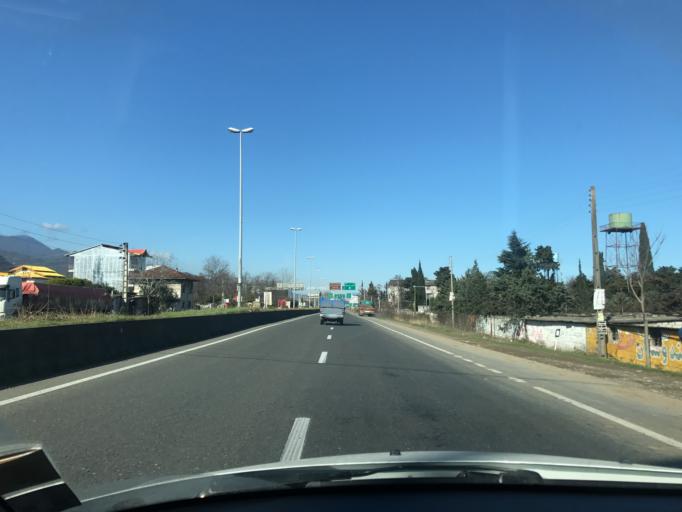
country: IR
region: Mazandaran
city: Ramsar
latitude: 36.9609
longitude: 50.5983
